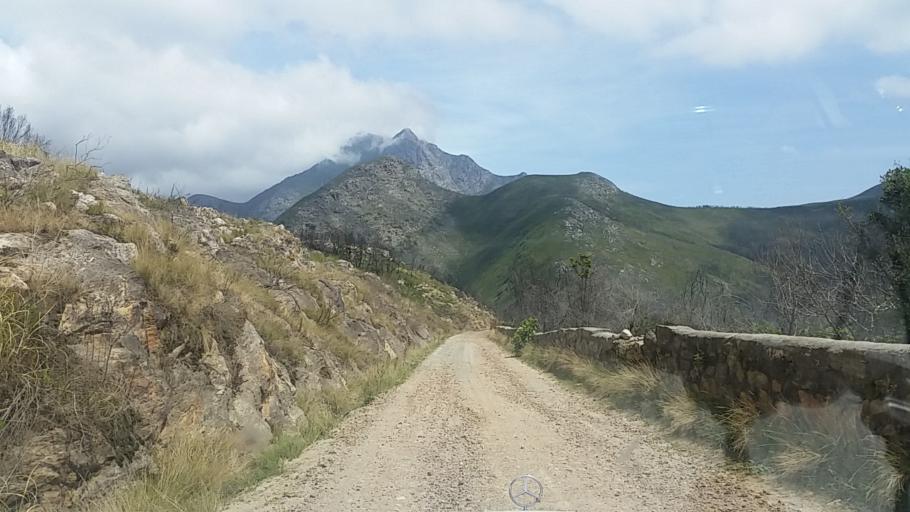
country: ZA
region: Western Cape
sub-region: Eden District Municipality
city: George
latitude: -33.8887
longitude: 22.4293
